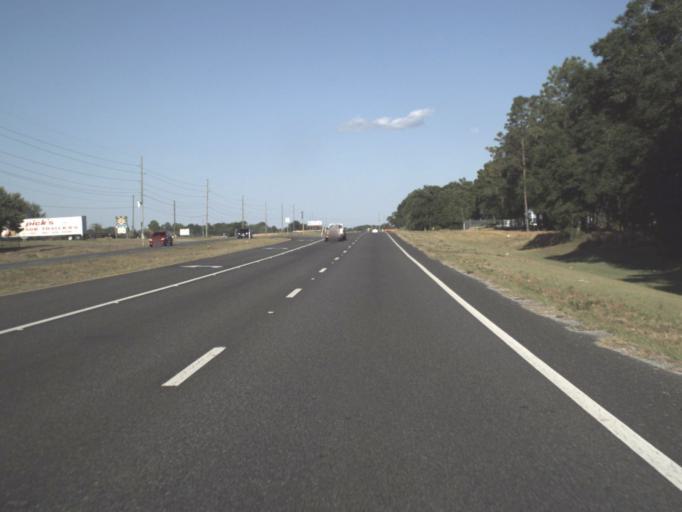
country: US
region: Florida
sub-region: Marion County
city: Ocala
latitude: 29.1863
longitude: -82.2303
